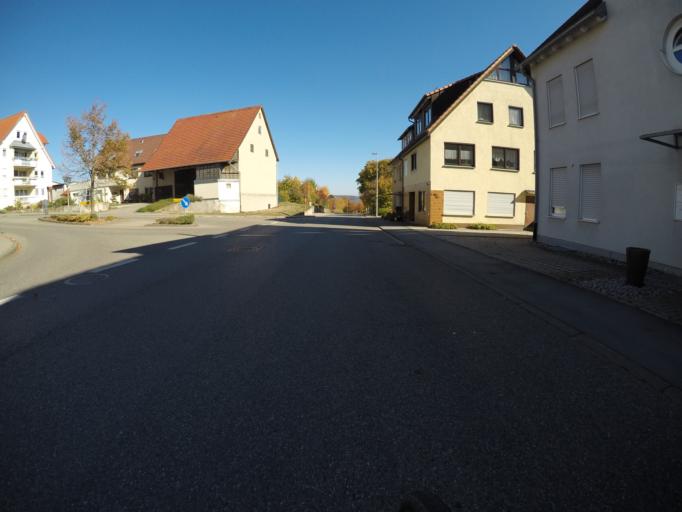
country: DE
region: Baden-Wuerttemberg
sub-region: Regierungsbezirk Stuttgart
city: Herrenberg
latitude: 48.5807
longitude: 8.8411
